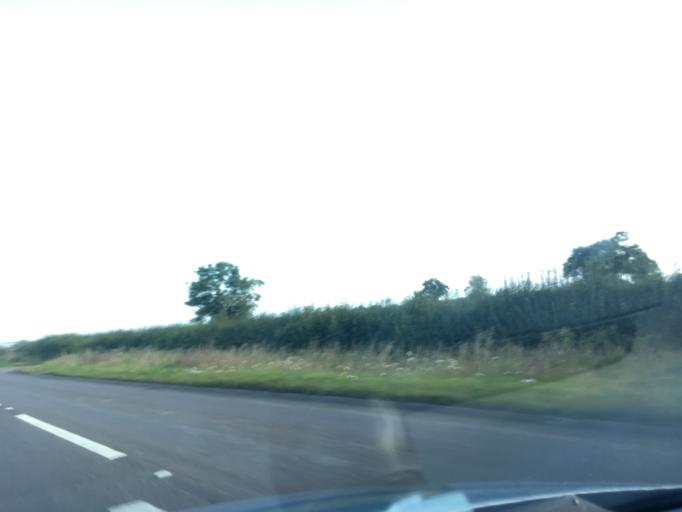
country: GB
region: England
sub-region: Oxfordshire
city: Banbury
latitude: 52.0755
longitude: -1.3115
